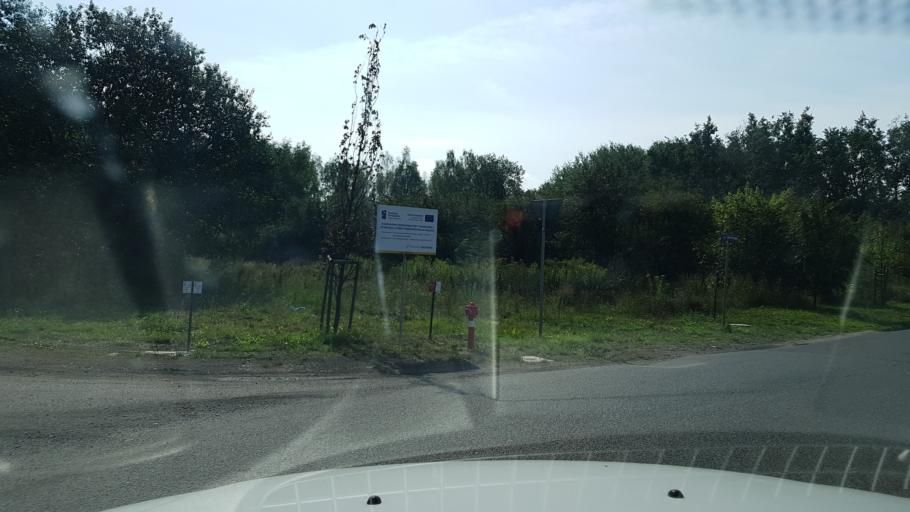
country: PL
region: West Pomeranian Voivodeship
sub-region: Powiat walecki
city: Walcz
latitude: 53.2729
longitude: 16.4933
